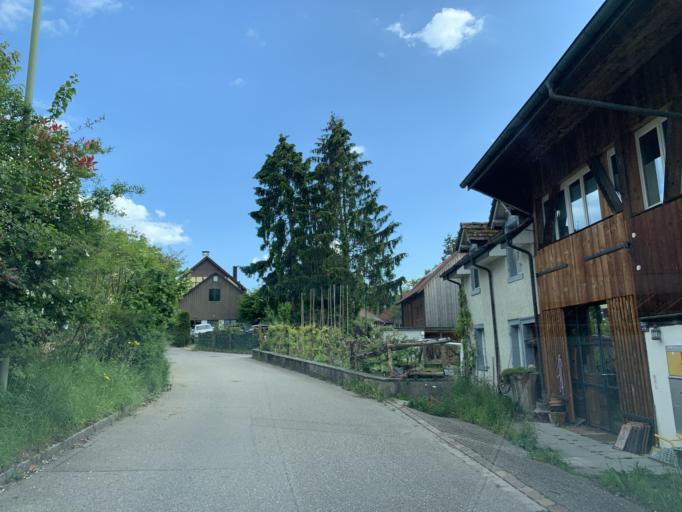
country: CH
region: Zurich
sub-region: Bezirk Winterthur
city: Wuelflingen (Kreis 6) / Niederfeld
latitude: 47.4973
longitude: 8.6761
